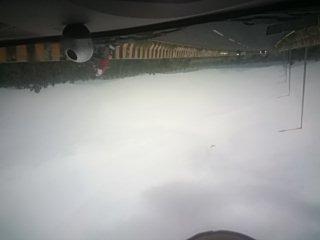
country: IN
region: Goa
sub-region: South Goa
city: Cavelossim
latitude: 15.1775
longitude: 73.9623
